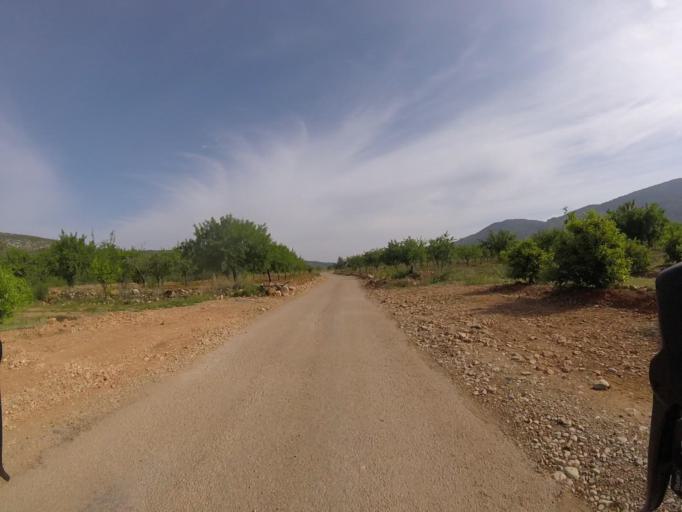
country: ES
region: Valencia
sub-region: Provincia de Castello
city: Alcala de Xivert
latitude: 40.2793
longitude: 0.2587
